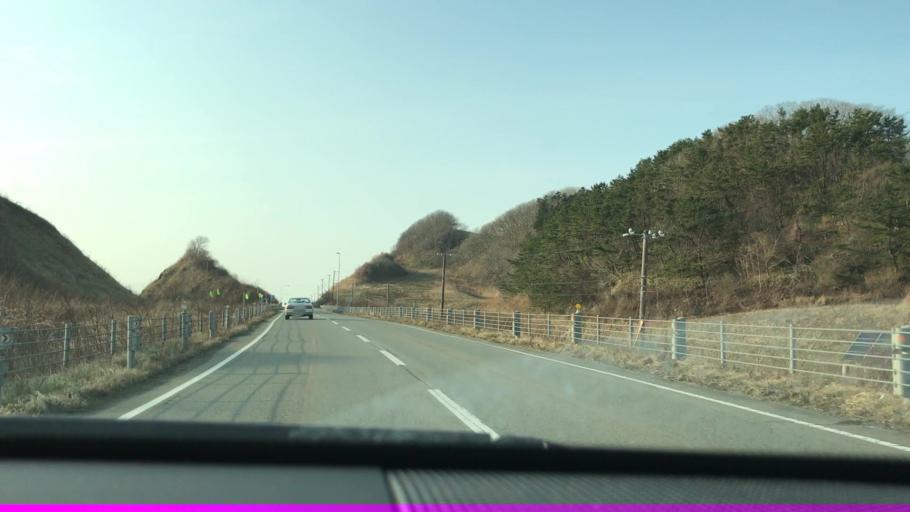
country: JP
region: Hokkaido
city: Shizunai-furukawacho
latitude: 42.2316
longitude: 142.6100
